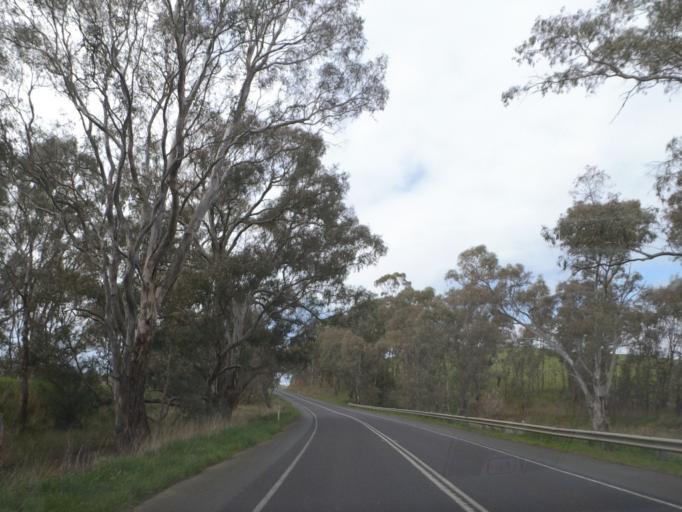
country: AU
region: Victoria
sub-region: Murrindindi
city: Kinglake West
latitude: -37.1643
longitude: 145.2938
